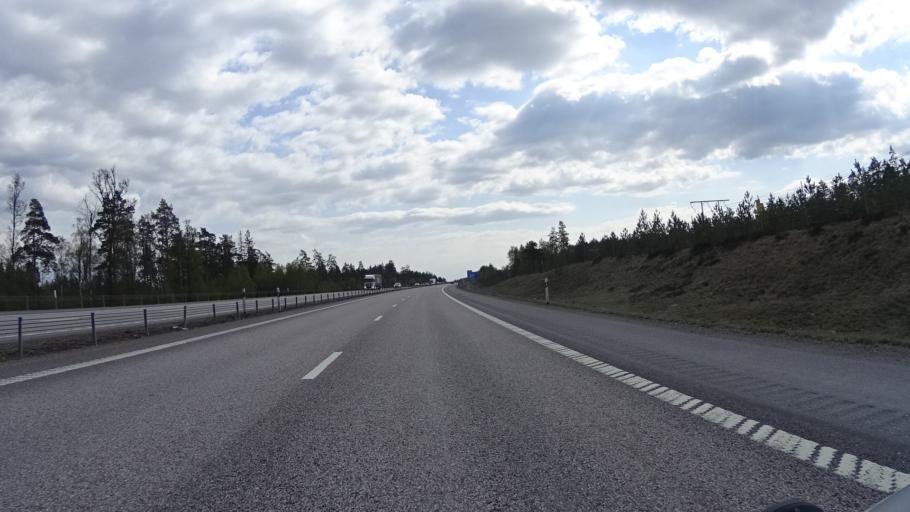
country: SE
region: Soedermanland
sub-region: Strangnas Kommun
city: Strangnas
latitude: 59.3479
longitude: 17.0092
